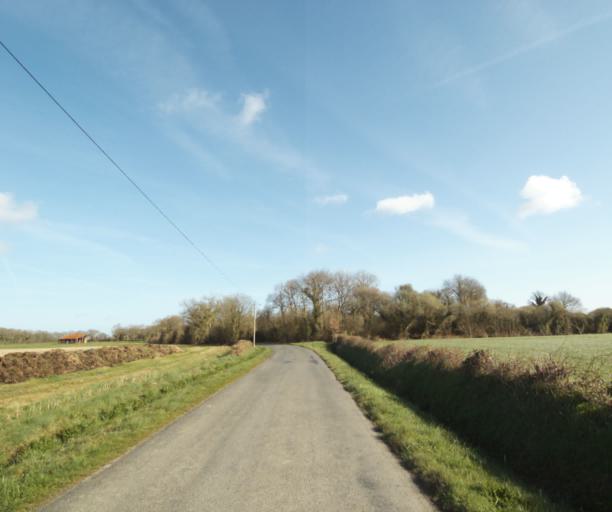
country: FR
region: Pays de la Loire
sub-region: Departement de la Loire-Atlantique
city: Bouvron
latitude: 47.3917
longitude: -1.8436
